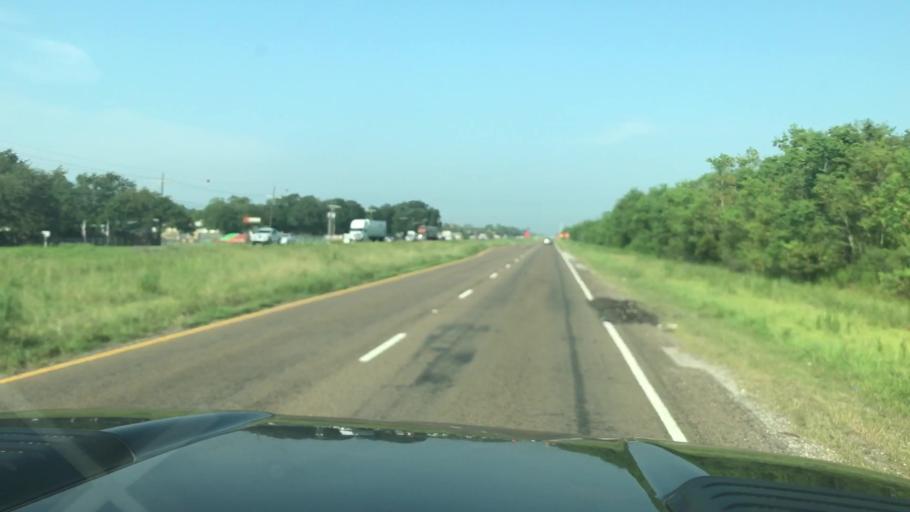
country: US
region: Texas
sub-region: Jefferson County
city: Bevil Oaks
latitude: 30.0647
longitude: -94.2113
